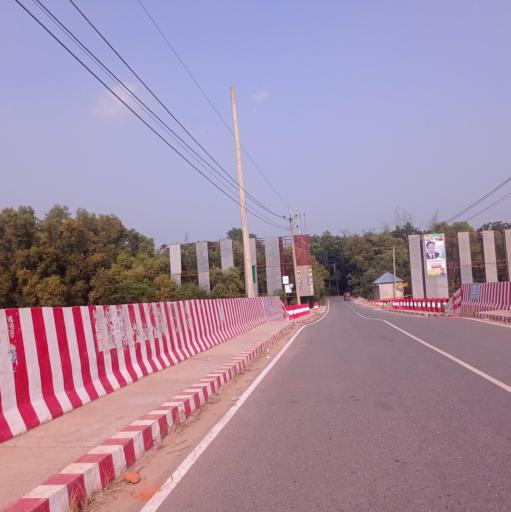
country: BD
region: Dhaka
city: Bhairab Bazar
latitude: 24.0548
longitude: 90.8358
